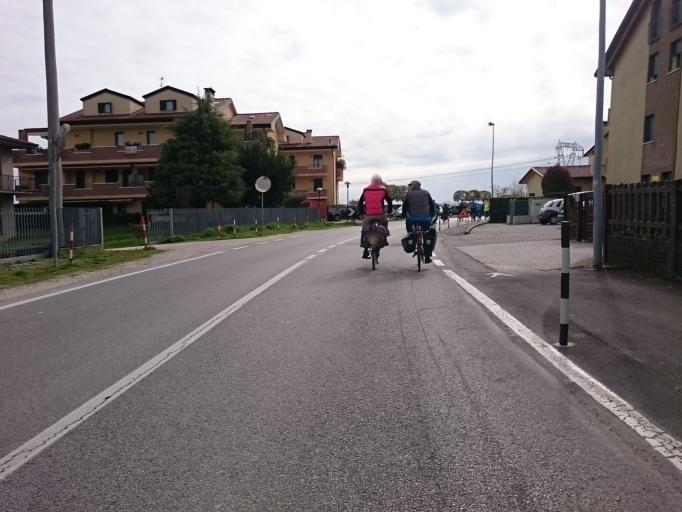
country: IT
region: Veneto
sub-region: Provincia di Padova
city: Mandriola-Sant'Agostino
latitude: 45.3609
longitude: 11.8496
